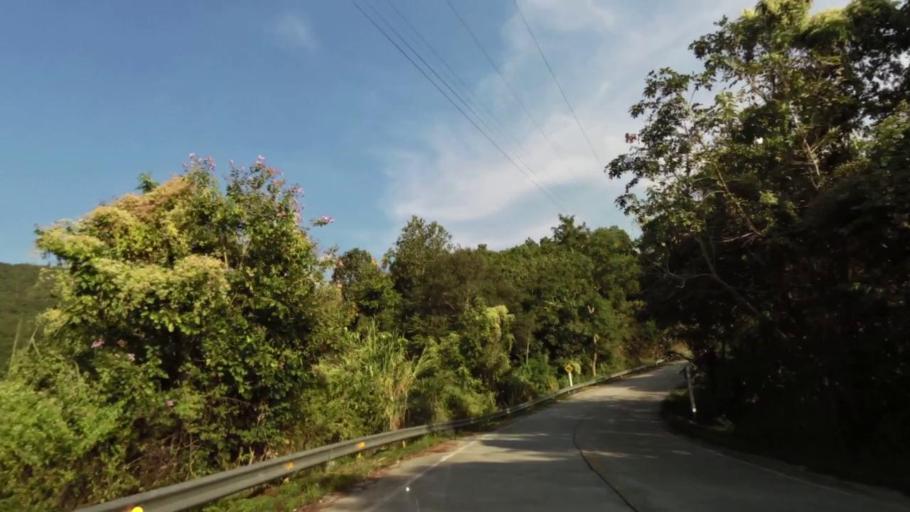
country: TH
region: Chiang Rai
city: Khun Tan
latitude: 19.8808
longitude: 100.3052
